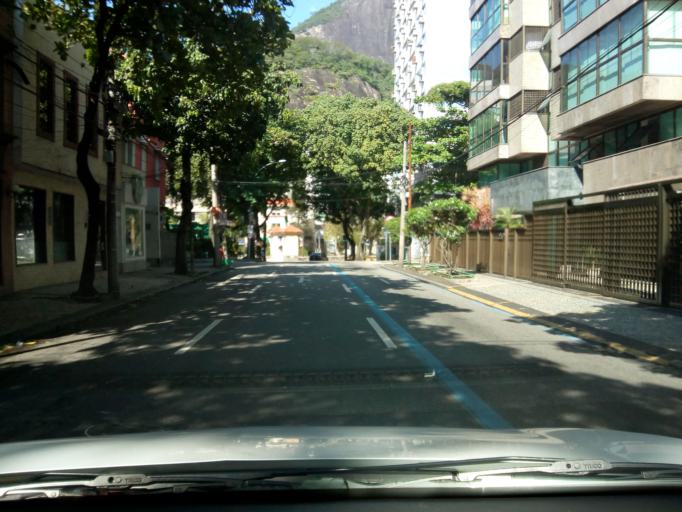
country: BR
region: Rio de Janeiro
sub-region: Rio De Janeiro
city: Rio de Janeiro
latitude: -22.9870
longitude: -43.2278
